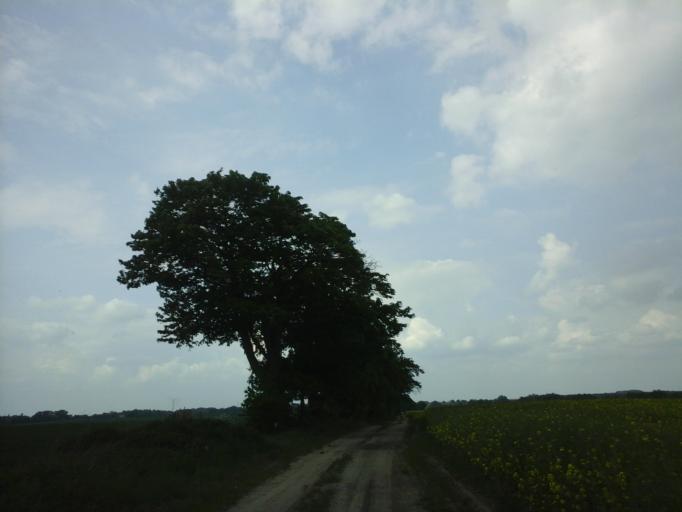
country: PL
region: West Pomeranian Voivodeship
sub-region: Powiat choszczenski
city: Pelczyce
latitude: 53.0738
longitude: 15.3189
